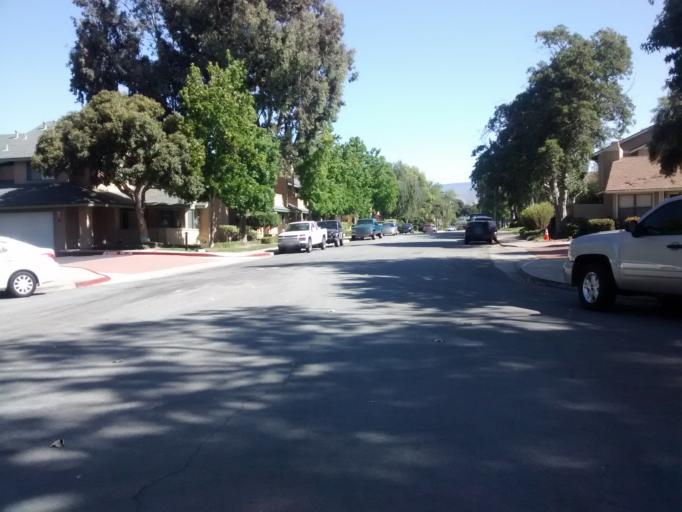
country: US
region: California
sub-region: San Luis Obispo County
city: San Luis Obispo
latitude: 35.2680
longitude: -120.6621
